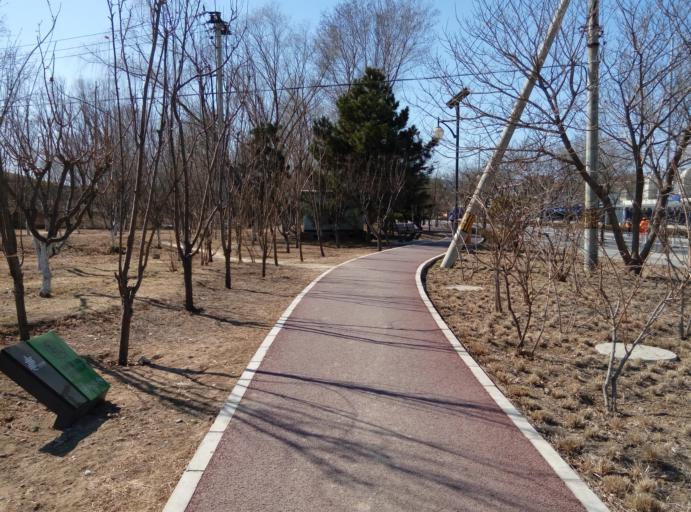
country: CN
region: Beijing
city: Haidian
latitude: 39.9889
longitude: 116.2859
